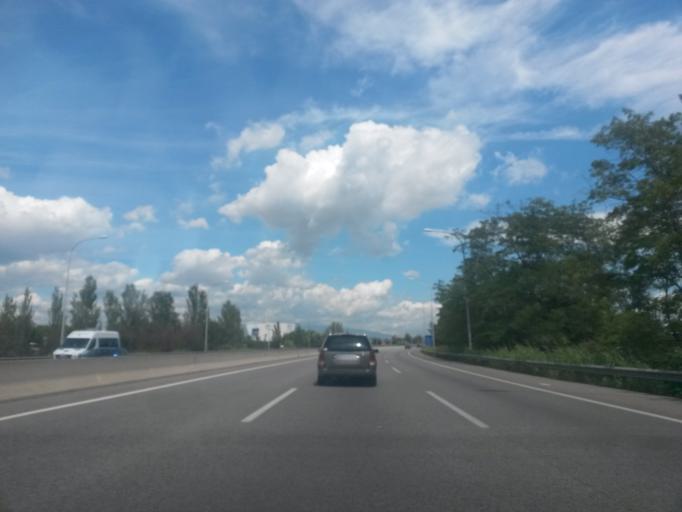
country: ES
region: Catalonia
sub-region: Provincia de Barcelona
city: Mollet del Valles
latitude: 41.5413
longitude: 2.2277
